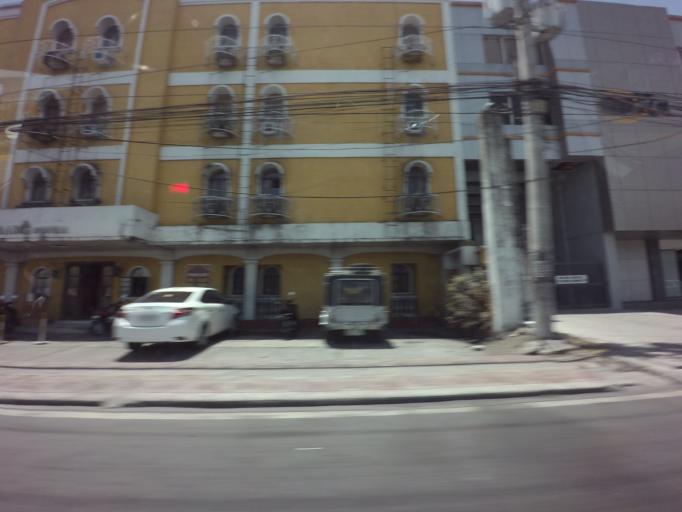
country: PH
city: Sambayanihan People's Village
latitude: 14.4913
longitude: 120.9921
